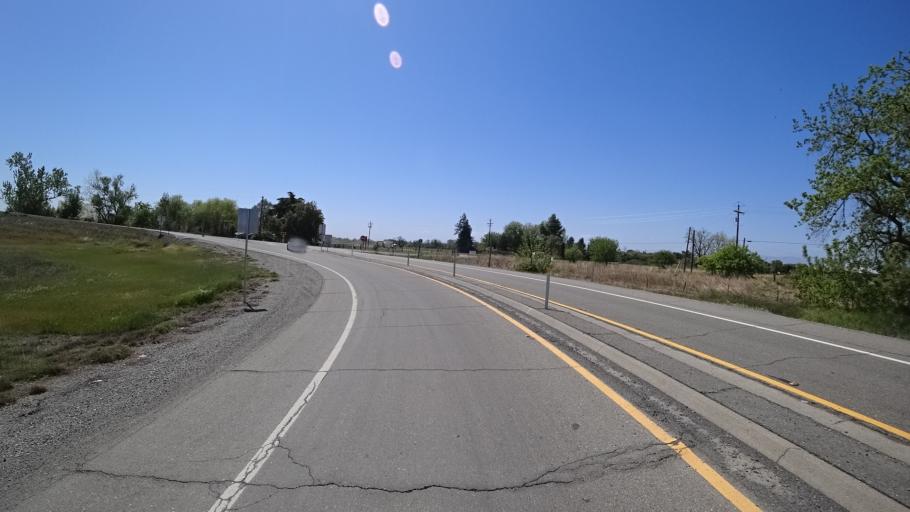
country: US
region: California
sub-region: Glenn County
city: Orland
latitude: 39.7845
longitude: -122.2059
